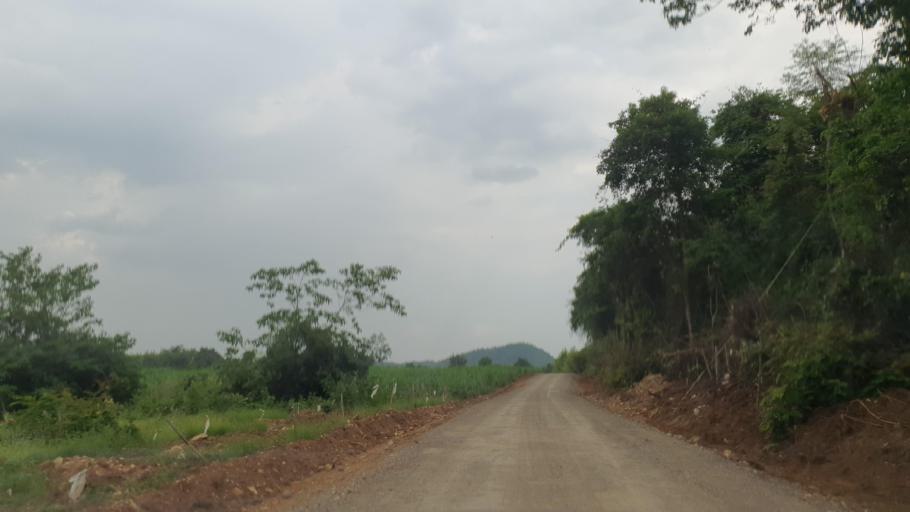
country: TH
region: Sukhothai
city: Thung Saliam
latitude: 17.2571
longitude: 99.5406
